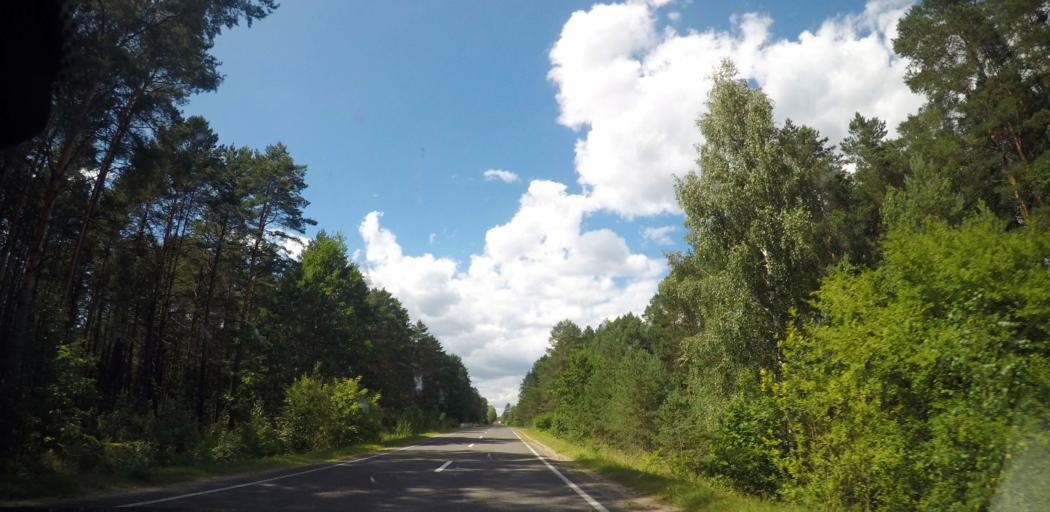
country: LT
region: Alytaus apskritis
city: Druskininkai
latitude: 53.8755
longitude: 24.1501
